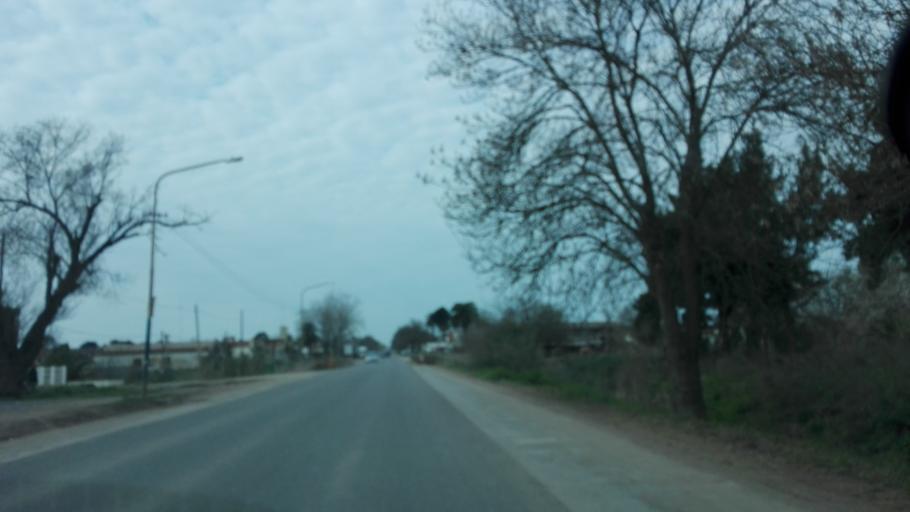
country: AR
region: Buenos Aires
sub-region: Partido de Chascomus
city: Chascomus
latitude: -35.5754
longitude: -57.9948
